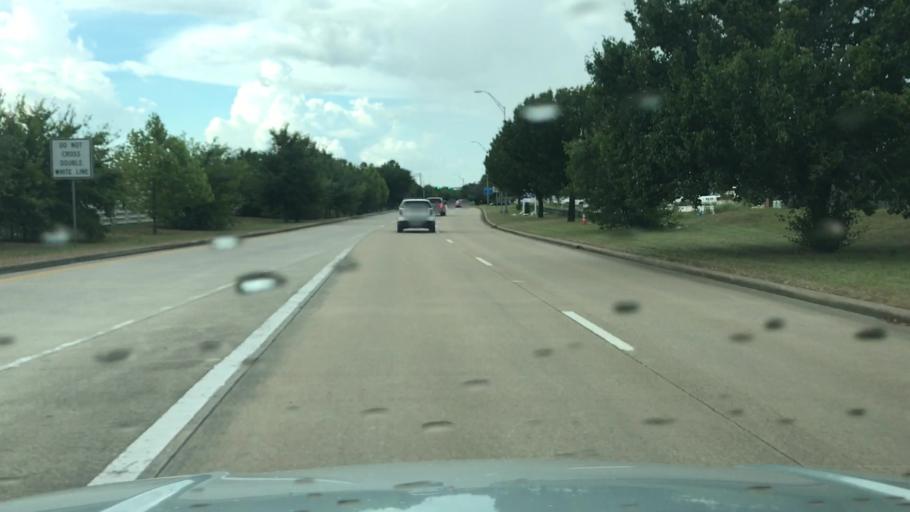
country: US
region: Texas
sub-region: Fort Bend County
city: Cinco Ranch
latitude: 29.7693
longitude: -95.7762
